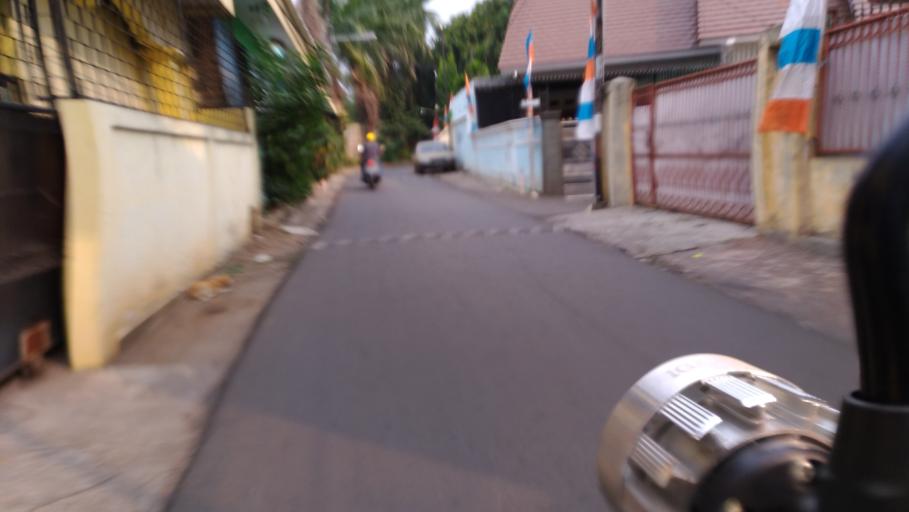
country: ID
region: West Java
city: Depok
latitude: -6.3541
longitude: 106.8831
